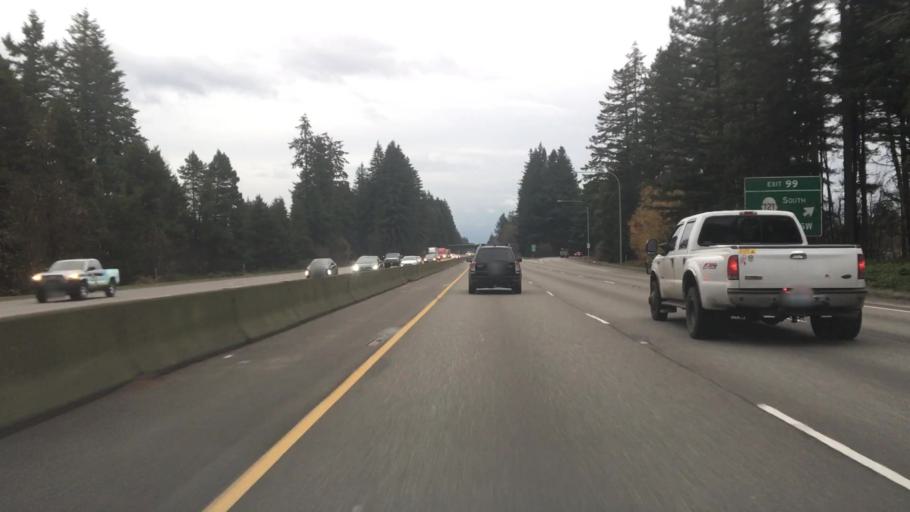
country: US
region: Washington
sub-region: Thurston County
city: Tumwater
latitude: 46.9579
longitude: -122.9360
